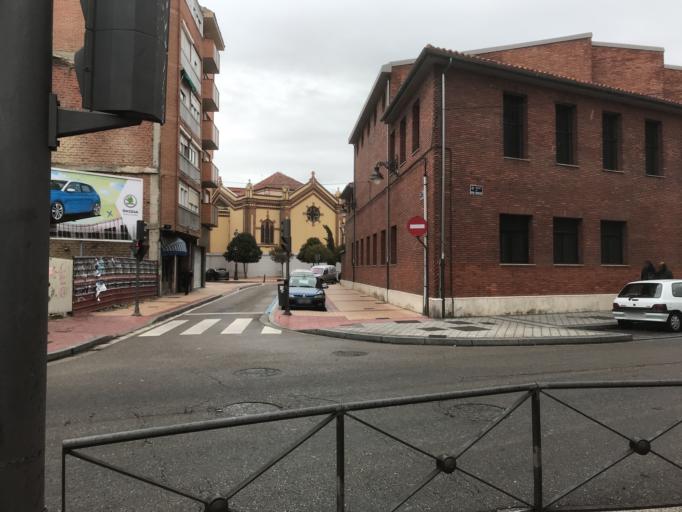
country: ES
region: Castille and Leon
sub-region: Provincia de Valladolid
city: Valladolid
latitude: 41.6507
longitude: -4.7175
